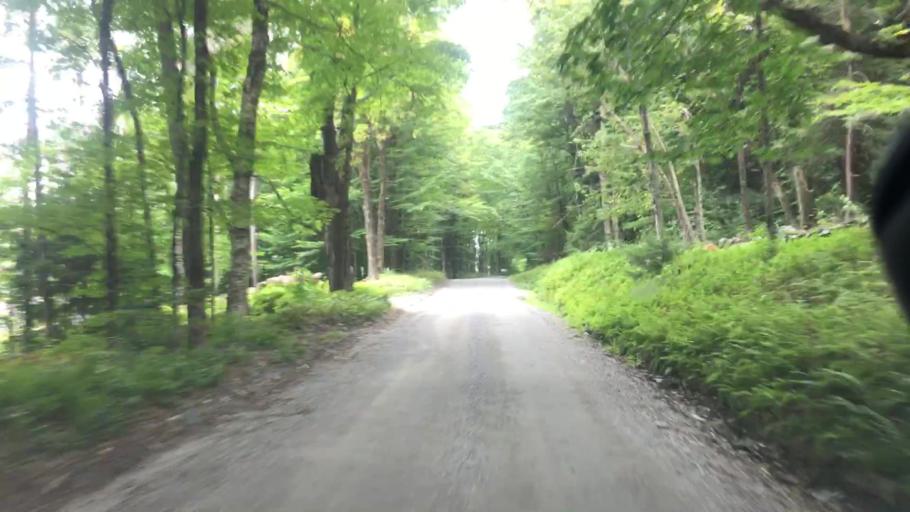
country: US
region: Vermont
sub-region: Windham County
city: Dover
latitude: 42.8412
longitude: -72.7675
